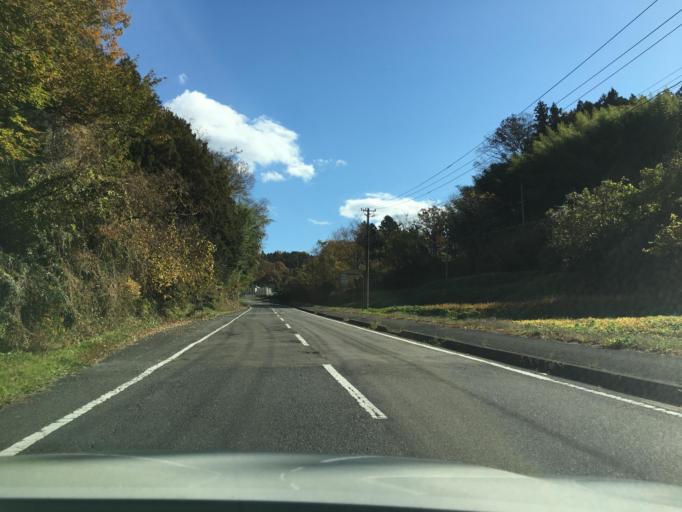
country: JP
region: Fukushima
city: Miharu
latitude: 37.4464
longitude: 140.4576
